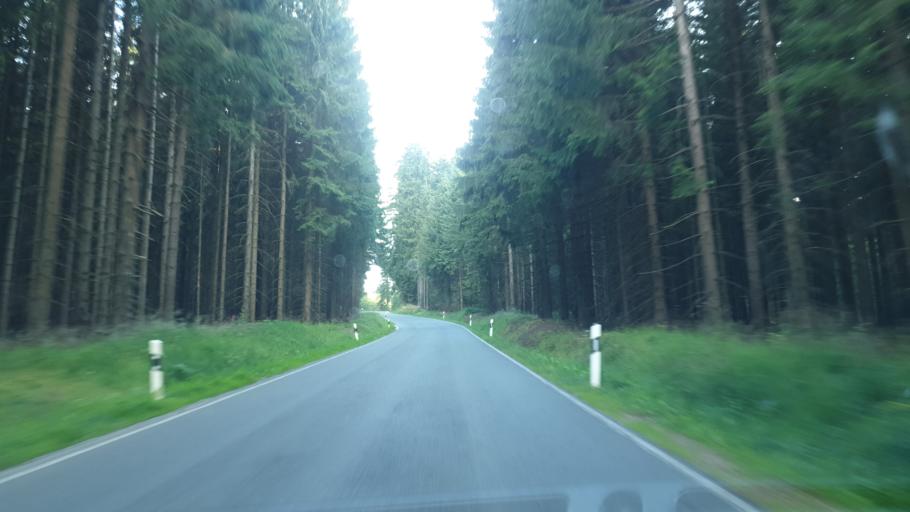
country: DE
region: Saxony
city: Tannenbergsthal
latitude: 50.4378
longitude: 12.4494
